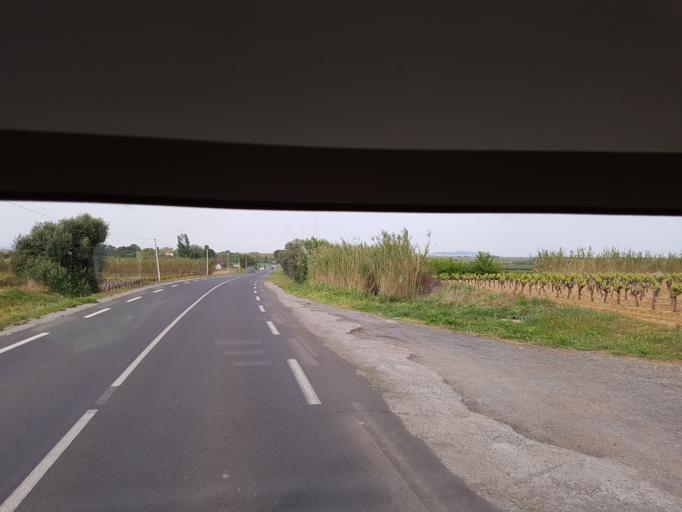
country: FR
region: Languedoc-Roussillon
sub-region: Departement de l'Herault
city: Agde
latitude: 43.3343
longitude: 3.4905
